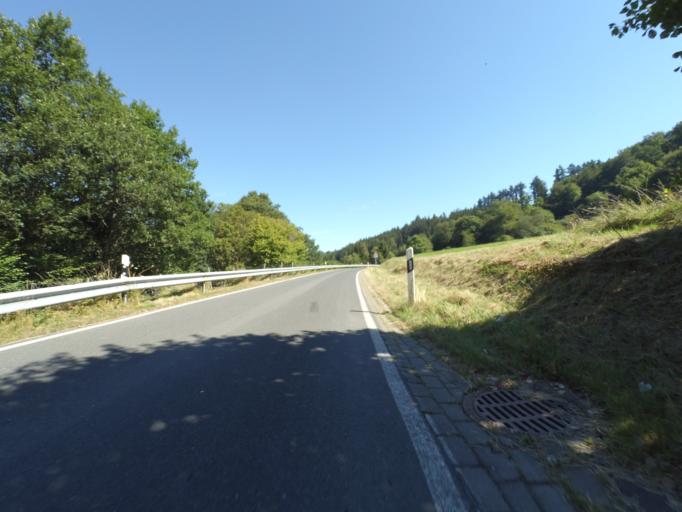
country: DE
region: Rheinland-Pfalz
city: Wagenhausen
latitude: 50.1491
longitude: 6.9713
